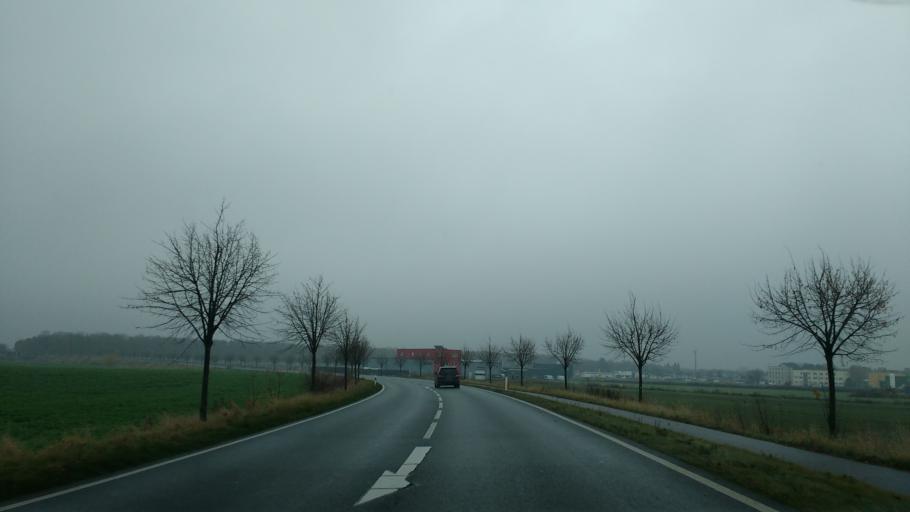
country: DE
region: North Rhine-Westphalia
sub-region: Regierungsbezirk Koln
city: Mengenich
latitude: 50.9518
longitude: 6.8420
